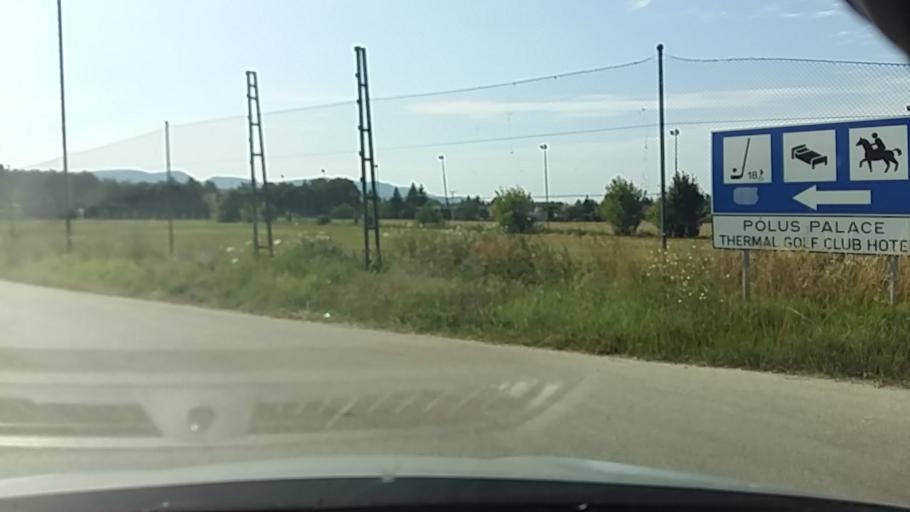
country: HU
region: Pest
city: God
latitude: 47.6946
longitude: 19.1567
